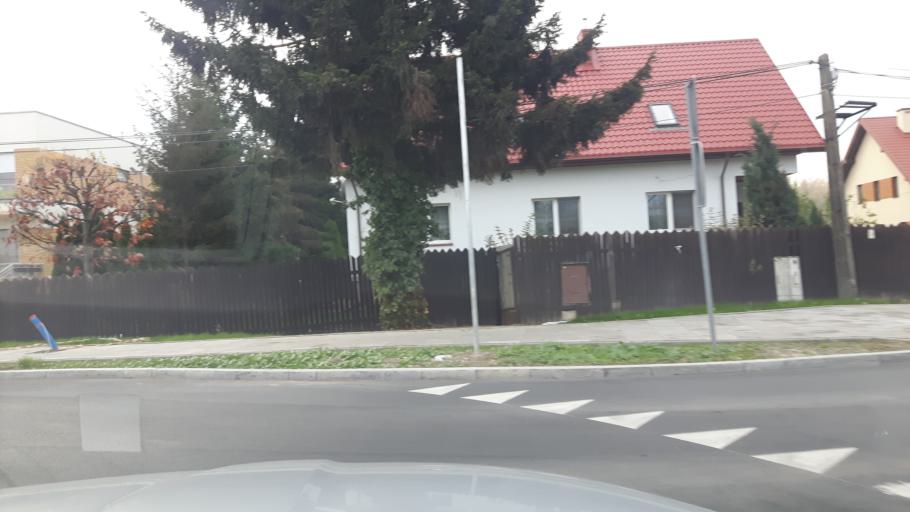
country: PL
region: Masovian Voivodeship
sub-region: Warszawa
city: Wilanow
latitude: 52.1738
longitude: 21.1083
